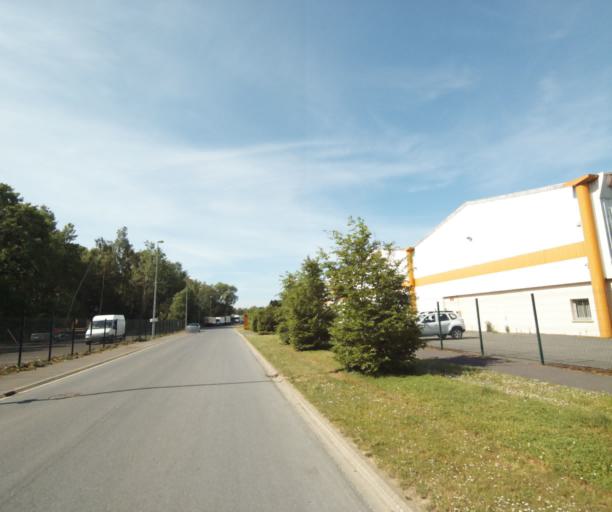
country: FR
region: Champagne-Ardenne
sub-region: Departement des Ardennes
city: Villers-Semeuse
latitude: 49.7383
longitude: 4.7294
